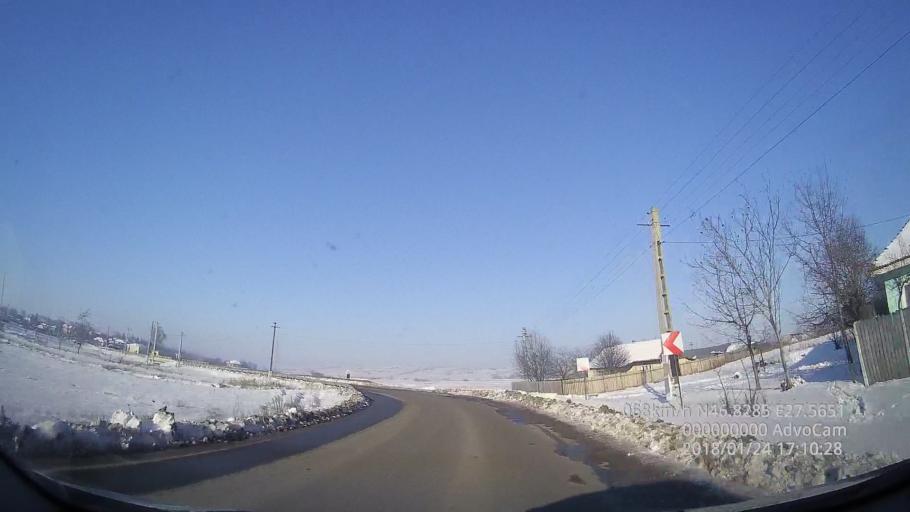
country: RO
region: Vaslui
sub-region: Comuna Vulturesti
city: Vulturesti
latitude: 46.8290
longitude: 27.5656
